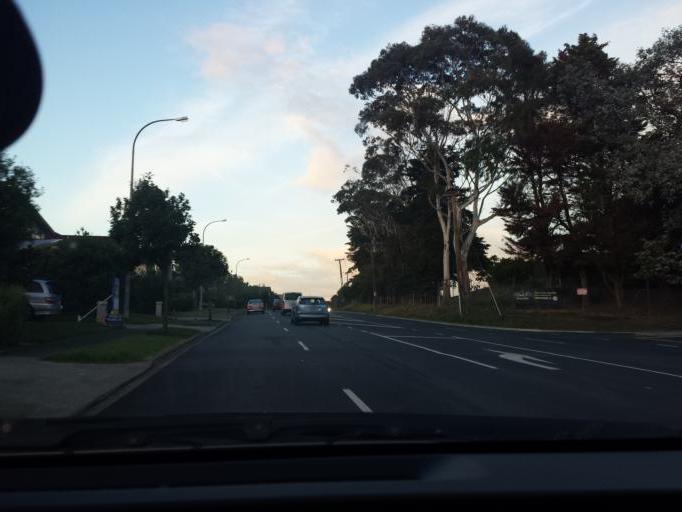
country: NZ
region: Auckland
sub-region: Auckland
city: Tamaki
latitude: -36.8829
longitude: 174.8378
